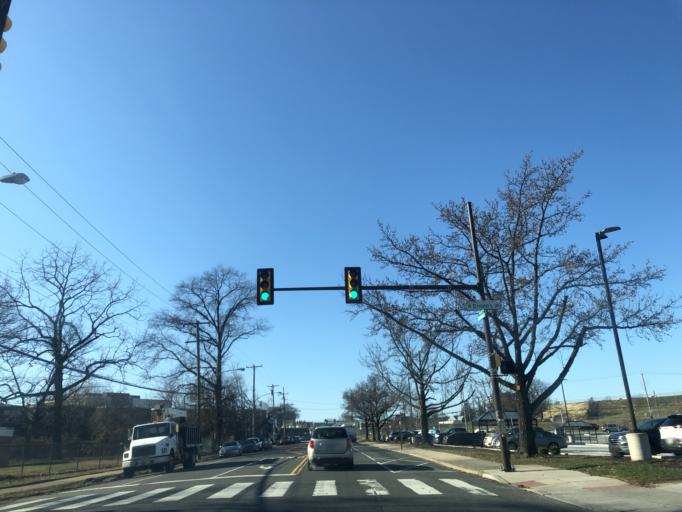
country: US
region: Pennsylvania
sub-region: Montgomery County
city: Bala-Cynwyd
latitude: 40.0018
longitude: -75.2133
